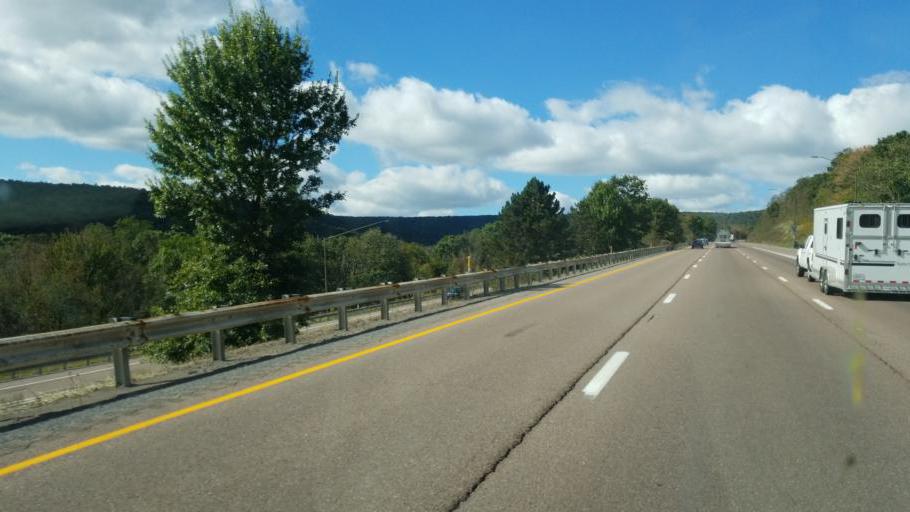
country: US
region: Maryland
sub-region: Allegany County
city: Frostburg
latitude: 39.6409
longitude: -78.9501
